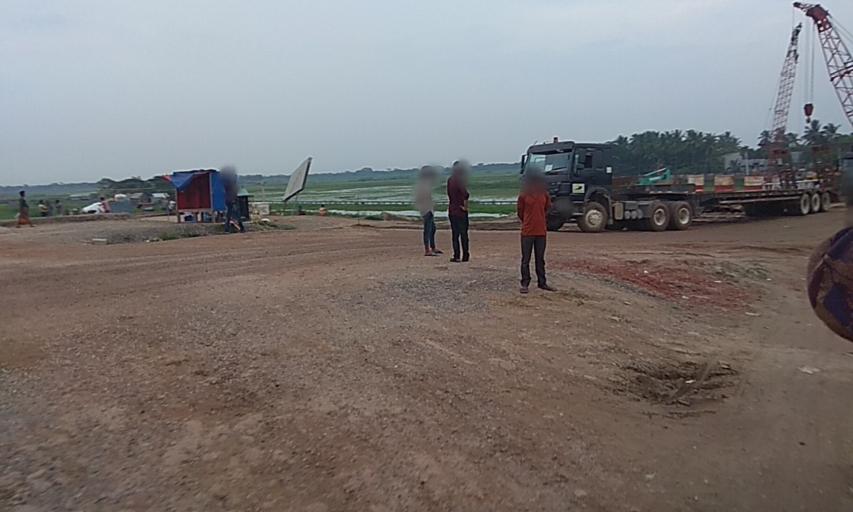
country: BD
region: Dhaka
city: Char Bhadrasan
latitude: 23.3886
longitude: 89.9869
